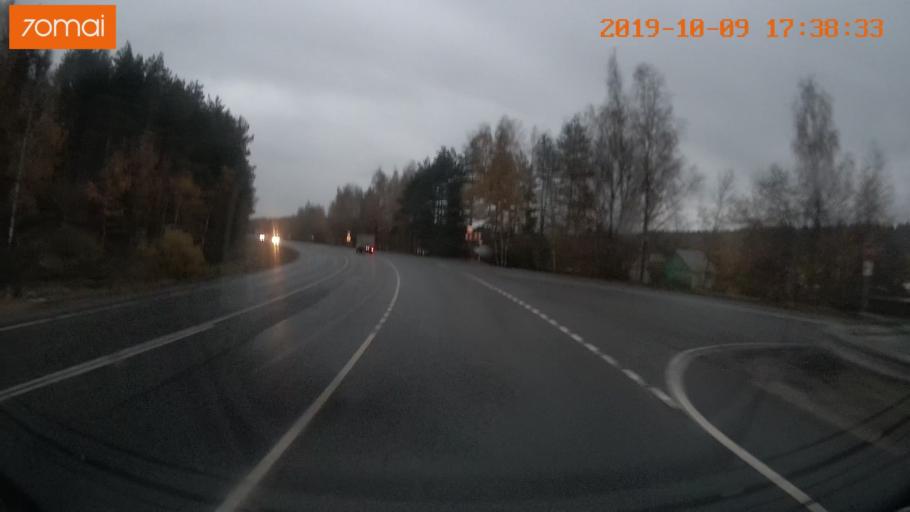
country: RU
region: Ivanovo
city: Bogorodskoye
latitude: 57.0701
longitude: 40.9516
